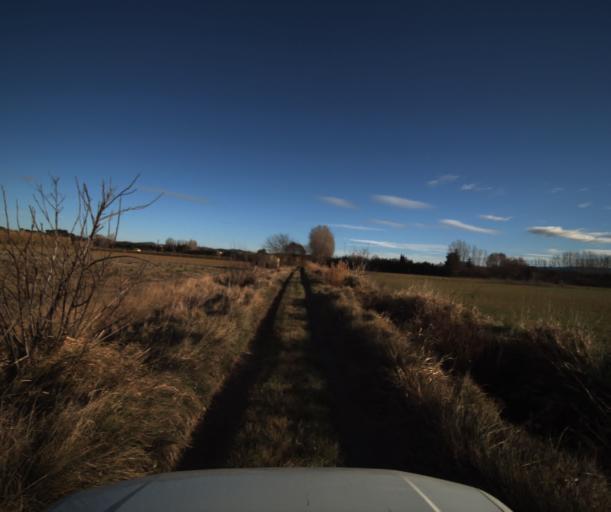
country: FR
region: Provence-Alpes-Cote d'Azur
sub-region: Departement du Vaucluse
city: Pertuis
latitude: 43.6925
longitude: 5.4688
